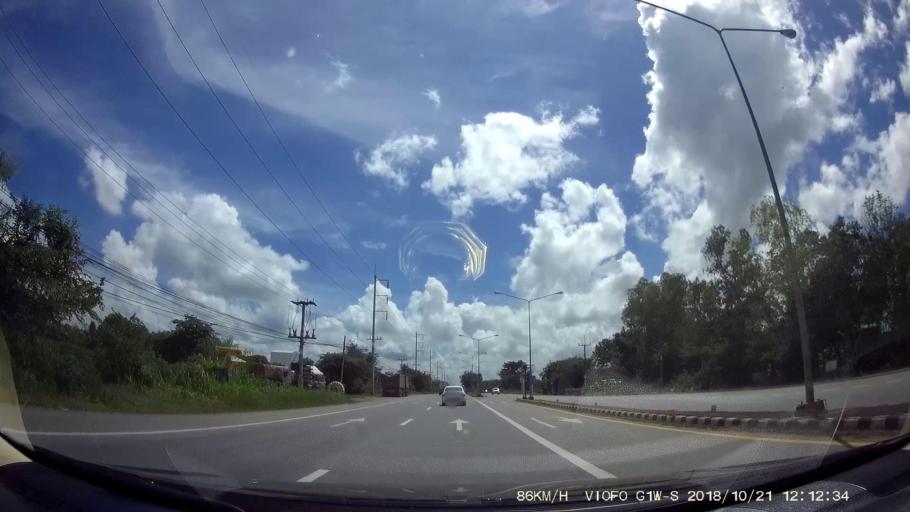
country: TH
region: Chaiyaphum
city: Chatturat
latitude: 15.4052
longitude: 101.8356
